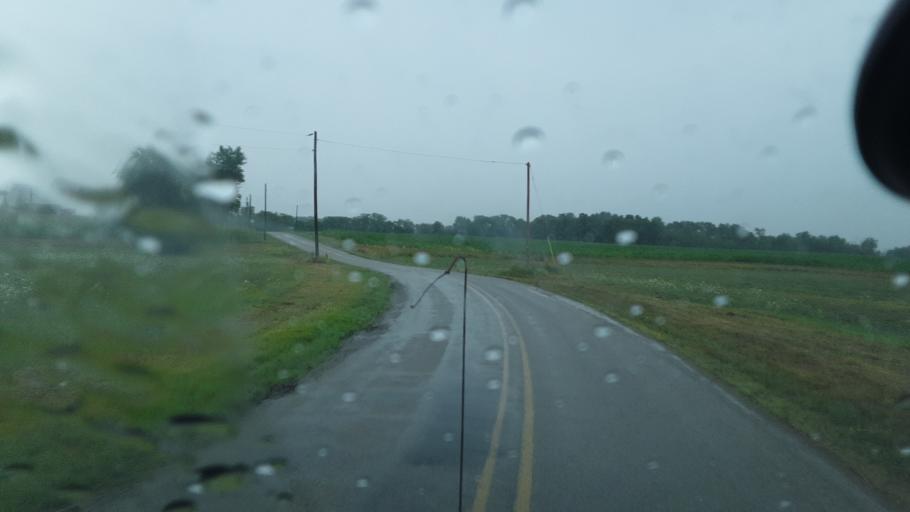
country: US
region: Indiana
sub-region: DeKalb County
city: Butler
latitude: 41.4448
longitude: -84.8137
